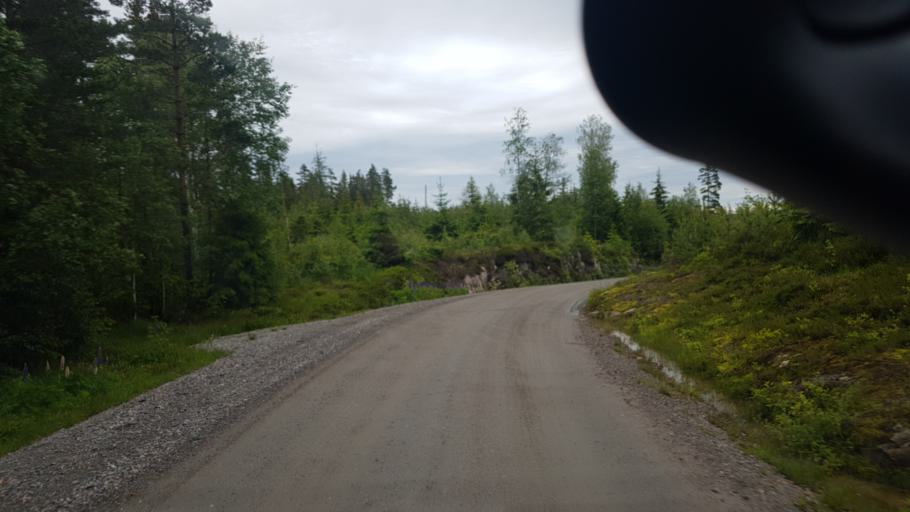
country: NO
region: Ostfold
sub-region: Romskog
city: Romskog
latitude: 59.7079
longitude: 12.0440
